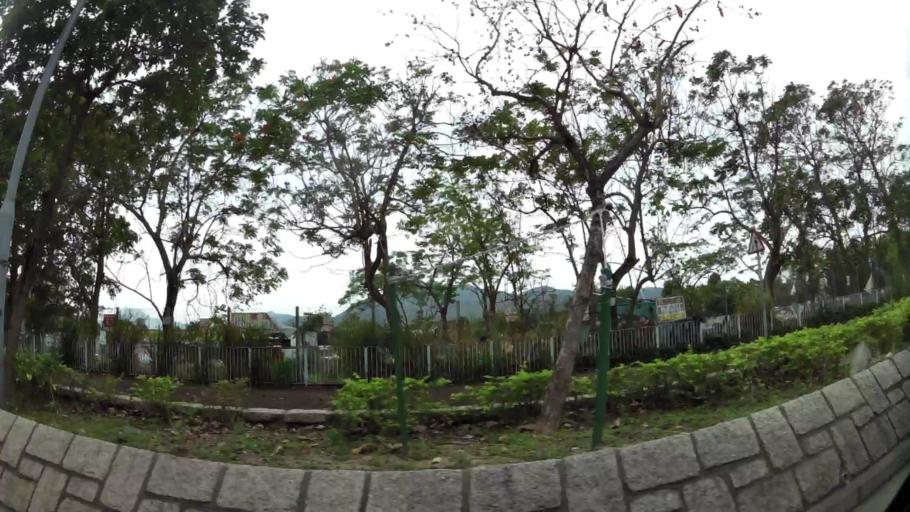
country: HK
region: Yuen Long
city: Yuen Long Kau Hui
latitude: 22.4379
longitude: 113.9963
